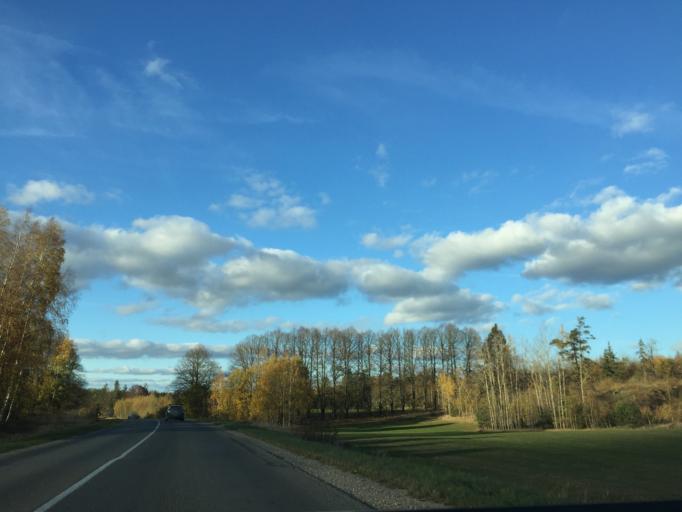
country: LV
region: Tukuma Rajons
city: Tukums
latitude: 56.9990
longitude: 23.0855
